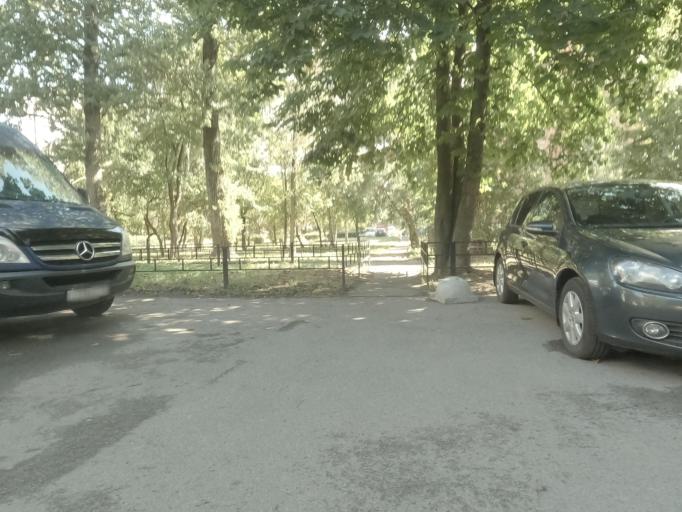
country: RU
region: St.-Petersburg
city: Centralniy
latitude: 59.9302
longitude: 30.4250
